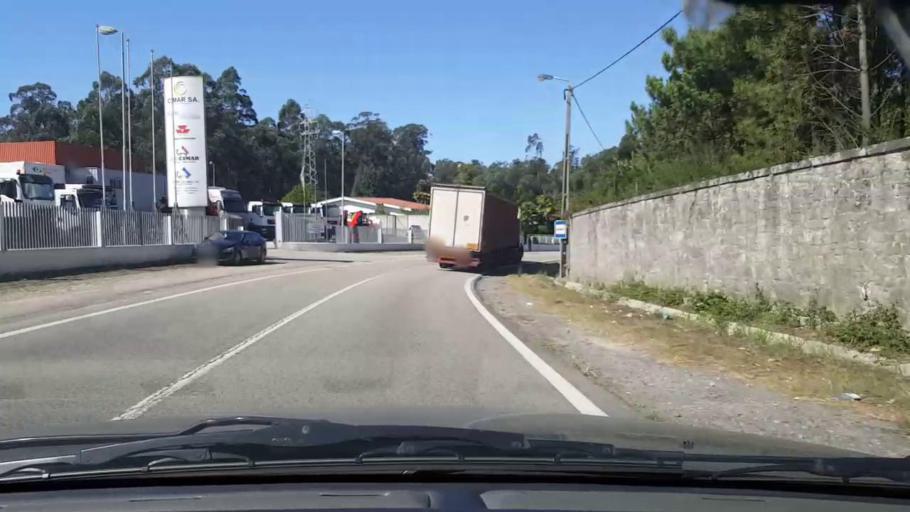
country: PT
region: Porto
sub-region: Vila do Conde
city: Arvore
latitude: 41.3383
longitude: -8.6905
